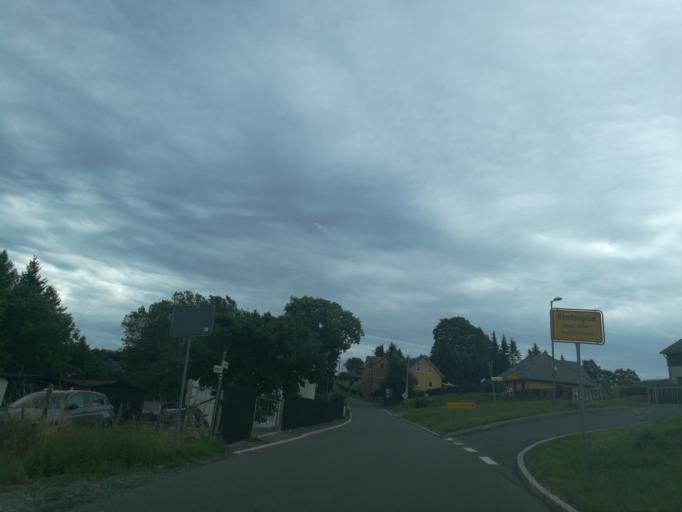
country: DE
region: Saxony
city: Adorf
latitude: 50.3118
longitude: 12.2683
